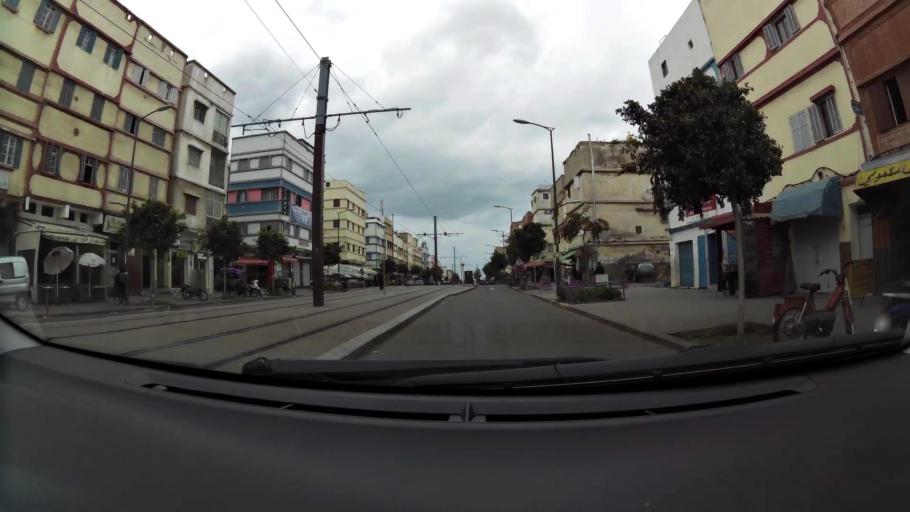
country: MA
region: Grand Casablanca
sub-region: Casablanca
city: Casablanca
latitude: 33.5871
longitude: -7.5672
